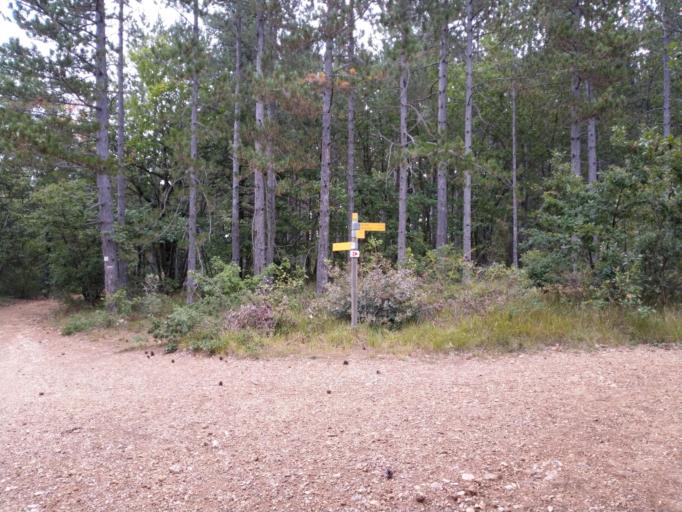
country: FR
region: Provence-Alpes-Cote d'Azur
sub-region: Departement du Vaucluse
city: Sault
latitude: 44.1147
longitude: 5.4240
